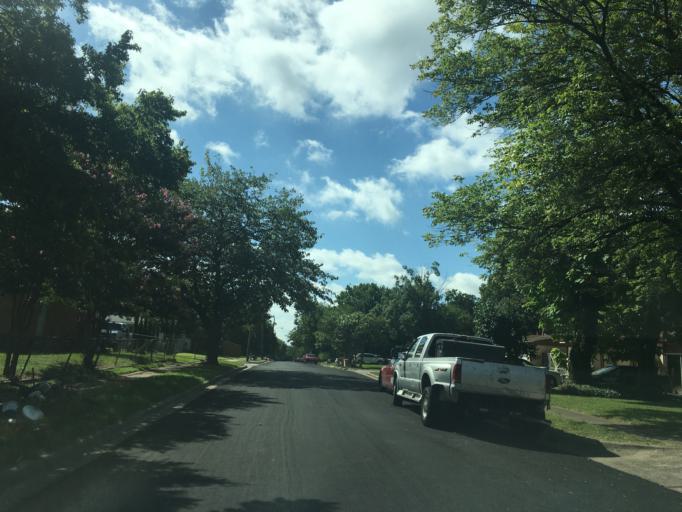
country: US
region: Texas
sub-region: Dallas County
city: Garland
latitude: 32.8424
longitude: -96.6600
